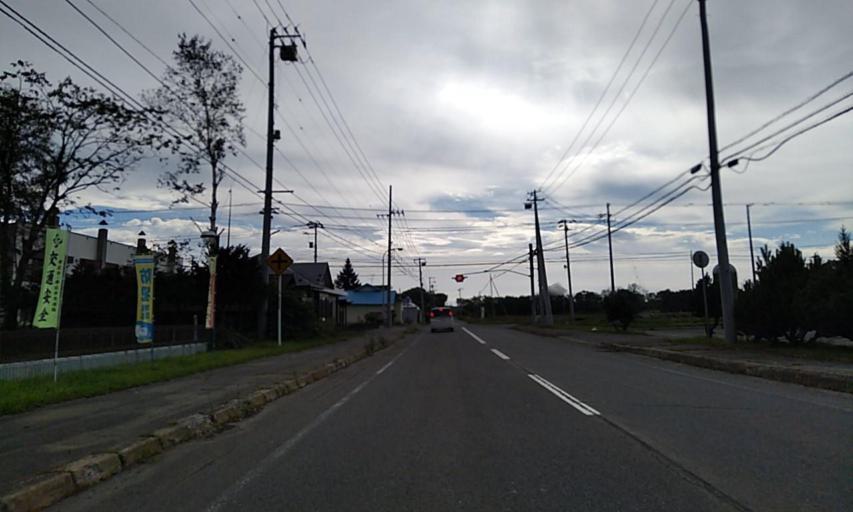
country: JP
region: Hokkaido
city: Obihiro
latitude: 42.8439
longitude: 143.1784
